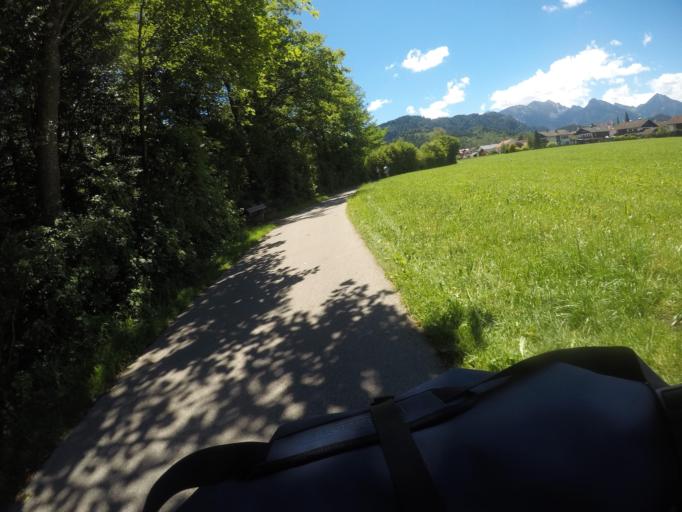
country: DE
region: Bavaria
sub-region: Swabia
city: Fuessen
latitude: 47.5737
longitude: 10.7119
